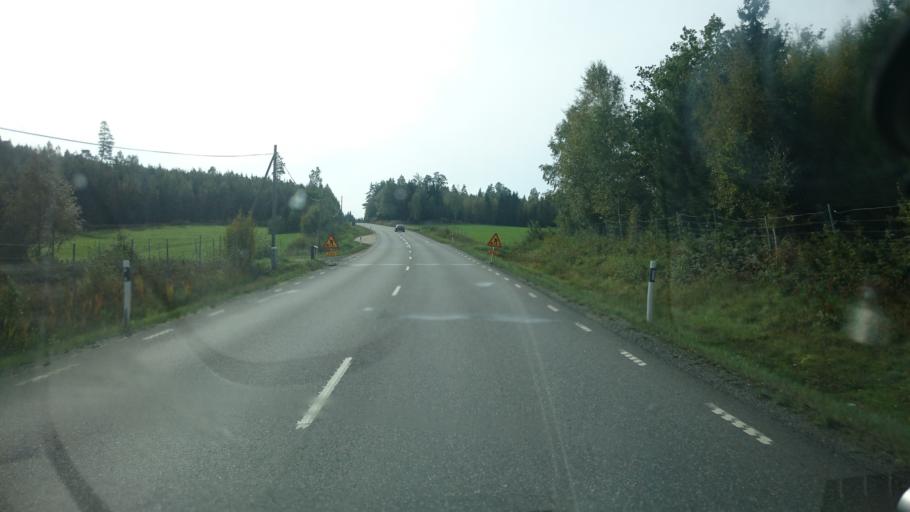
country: SE
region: Vaestra Goetaland
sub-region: Alingsas Kommun
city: Alingsas
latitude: 58.0053
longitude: 12.4438
